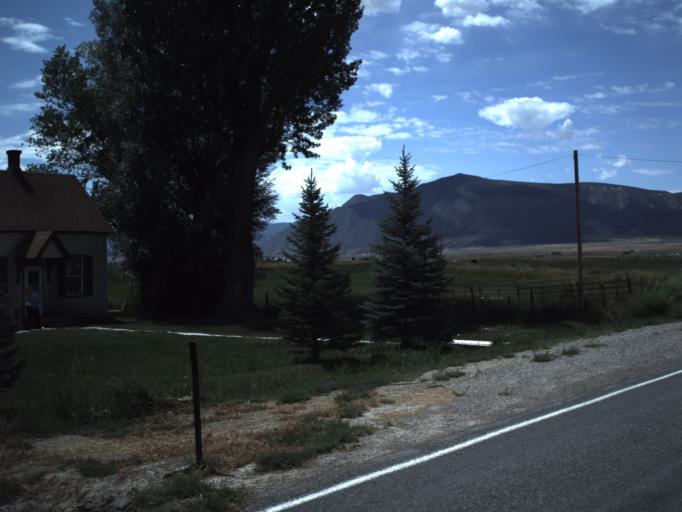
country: US
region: Utah
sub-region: Sanpete County
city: Moroni
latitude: 39.4759
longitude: -111.5768
